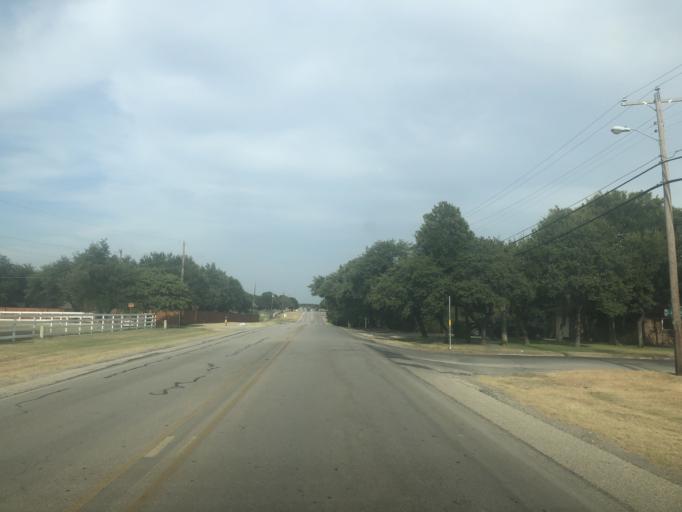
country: US
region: Texas
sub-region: Tarrant County
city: Lakeside
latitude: 32.8231
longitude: -97.4937
